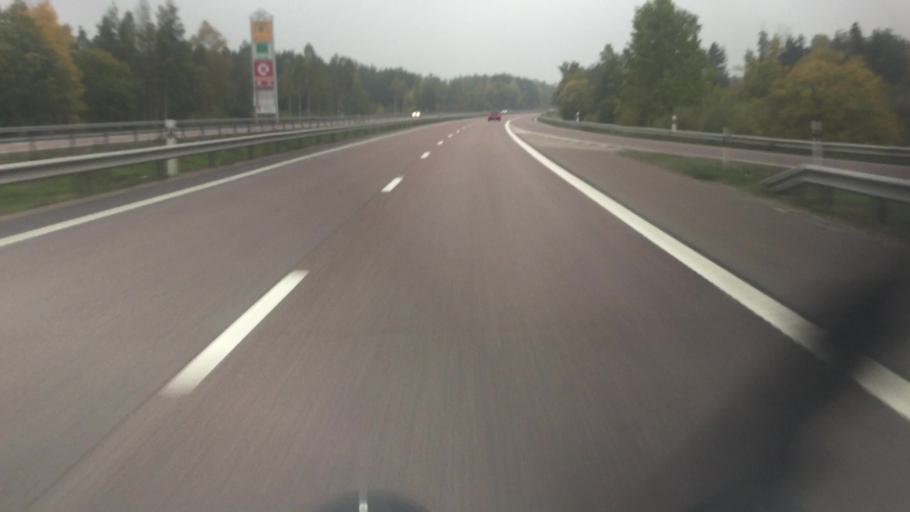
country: SE
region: Gaevleborg
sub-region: Gavle Kommun
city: Gavle
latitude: 60.6510
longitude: 17.1171
